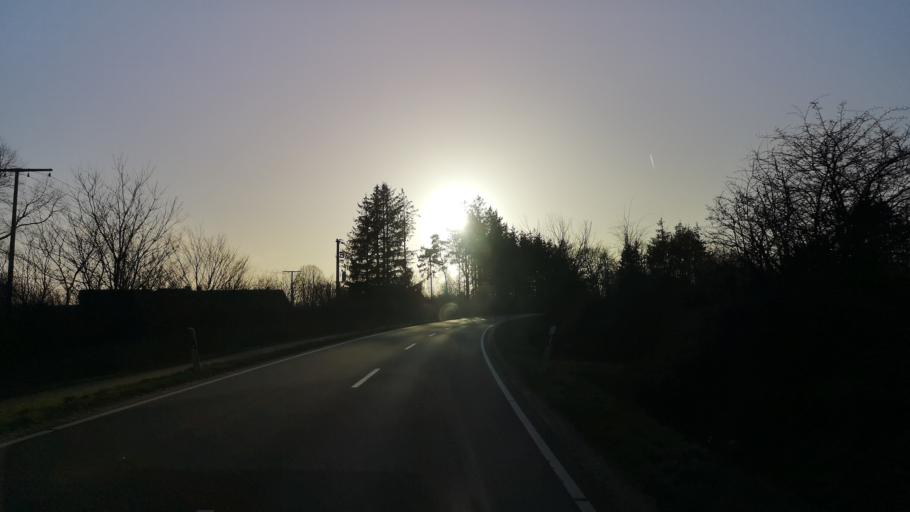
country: DE
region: Schleswig-Holstein
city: Sieverstedt
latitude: 54.6805
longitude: 9.4902
